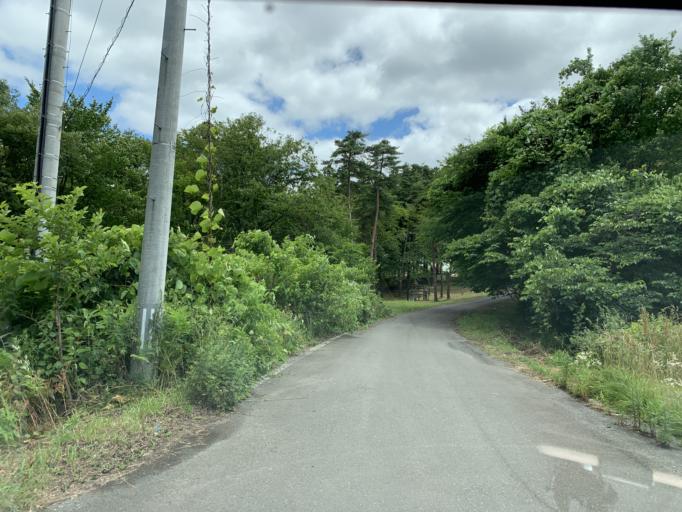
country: JP
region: Iwate
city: Ichinoseki
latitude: 38.9248
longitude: 141.0755
